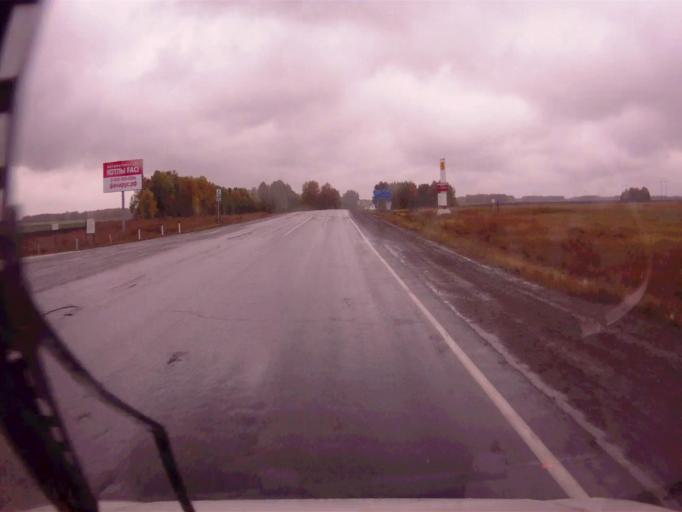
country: RU
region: Chelyabinsk
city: Roshchino
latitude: 55.3940
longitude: 61.1066
